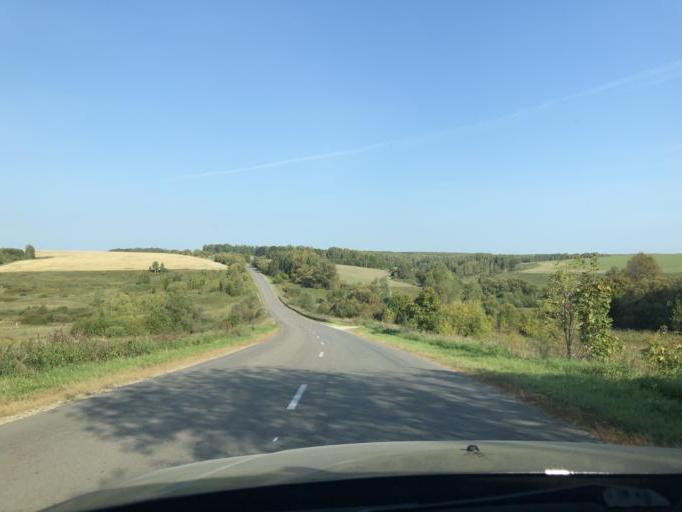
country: RU
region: Tula
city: Novogurovskiy
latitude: 54.3553
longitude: 37.3520
